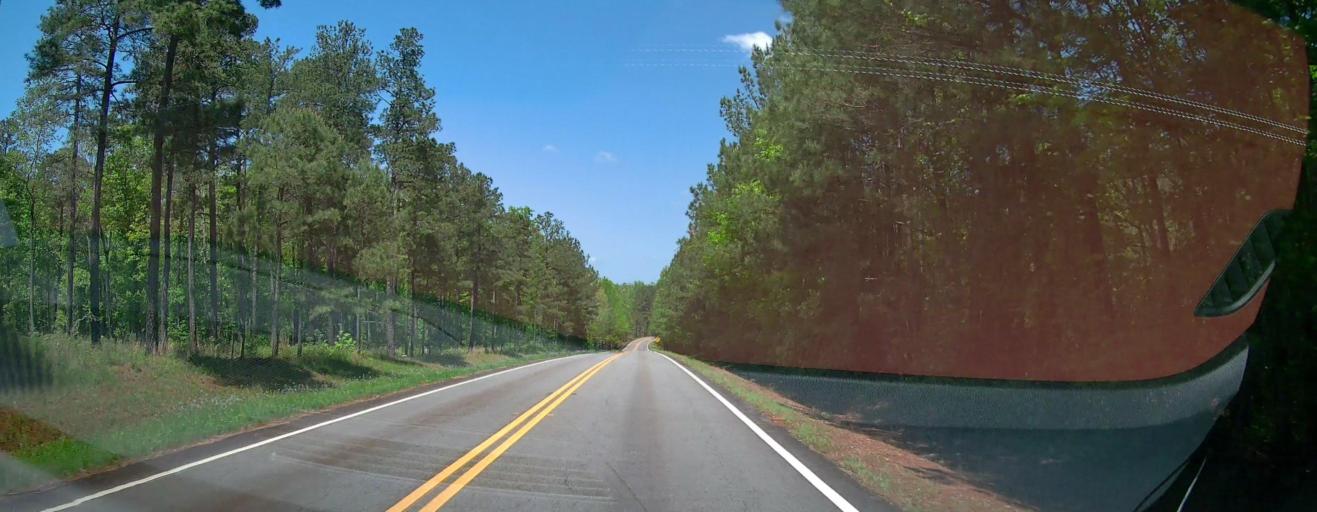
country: US
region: Georgia
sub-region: Jones County
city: Gray
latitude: 33.1302
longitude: -83.6302
